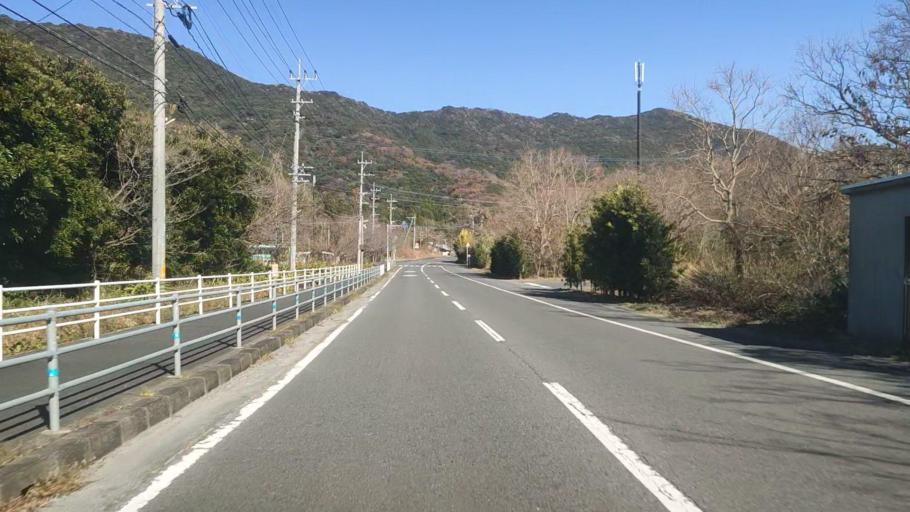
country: JP
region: Oita
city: Saiki
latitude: 32.8018
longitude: 131.9432
